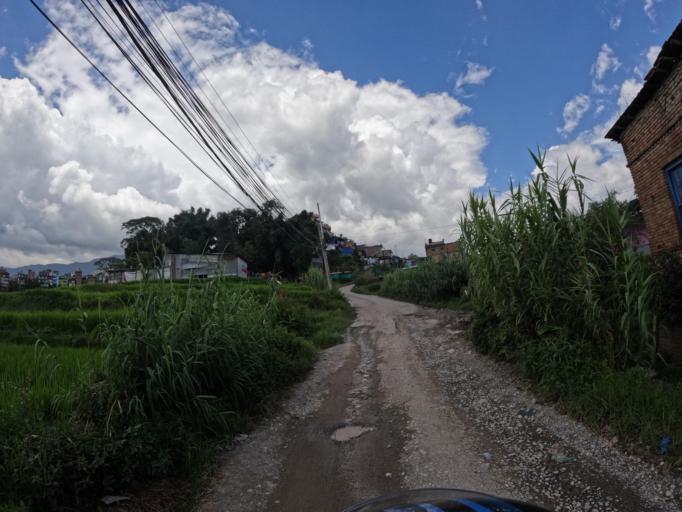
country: NP
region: Central Region
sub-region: Bagmati Zone
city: Kathmandu
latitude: 27.7659
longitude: 85.3280
